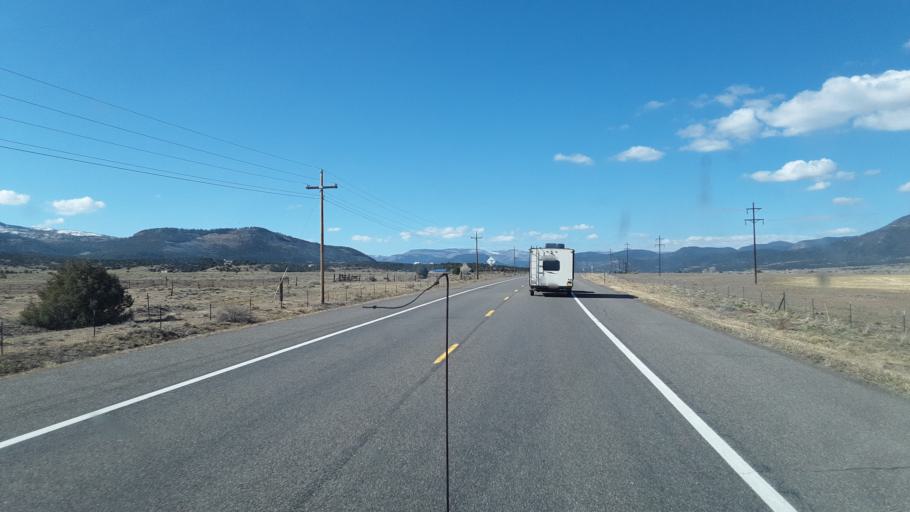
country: US
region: Colorado
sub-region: Rio Grande County
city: Del Norte
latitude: 37.6773
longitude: -106.4952
